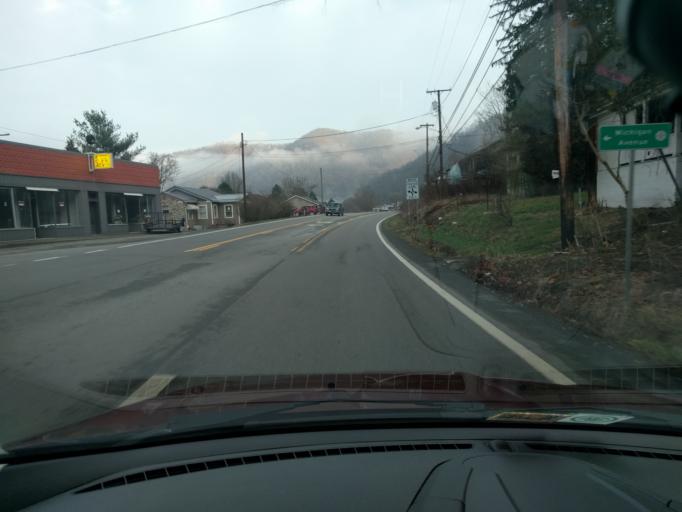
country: US
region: West Virginia
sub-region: Kanawha County
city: Montgomery
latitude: 38.1717
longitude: -81.3036
